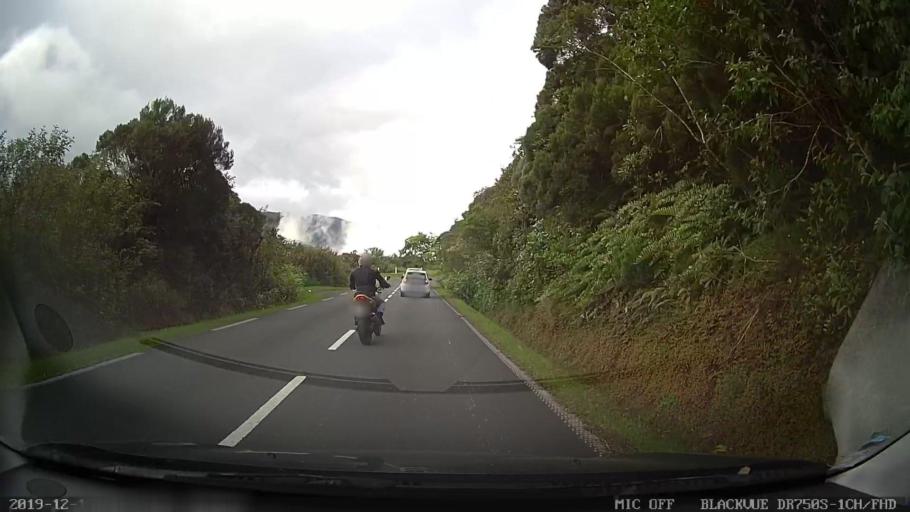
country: RE
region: Reunion
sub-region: Reunion
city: Cilaos
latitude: -21.1611
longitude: 55.5954
